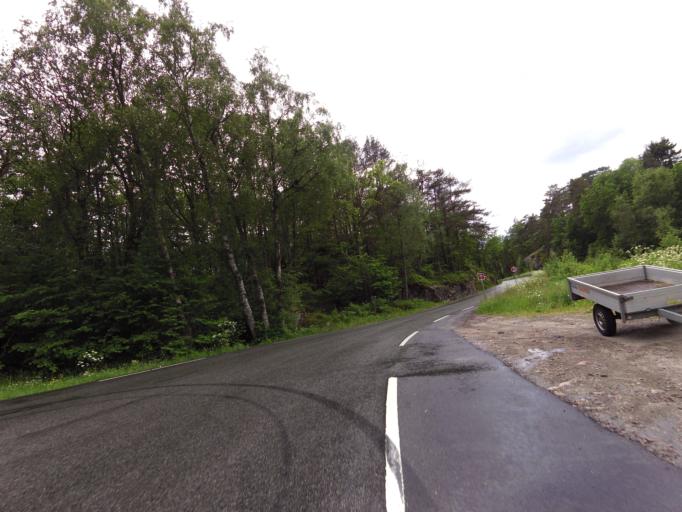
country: NO
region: Vest-Agder
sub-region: Mandal
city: Mandal
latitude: 58.0175
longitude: 7.5153
